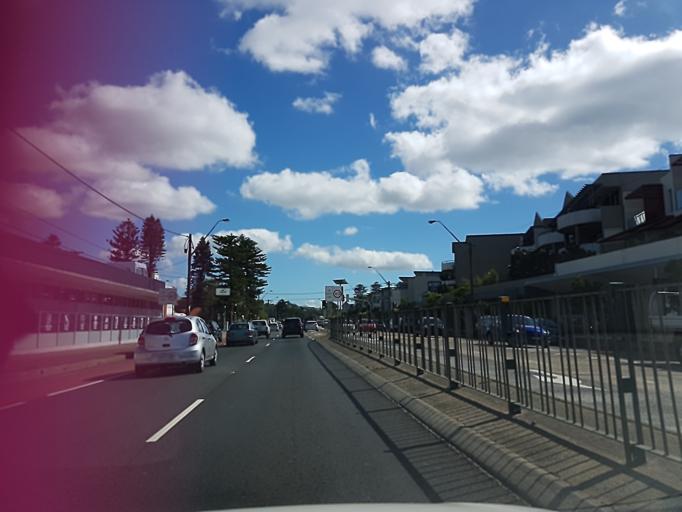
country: AU
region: New South Wales
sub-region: Warringah
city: Narrabeen
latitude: -33.7194
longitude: 151.2979
